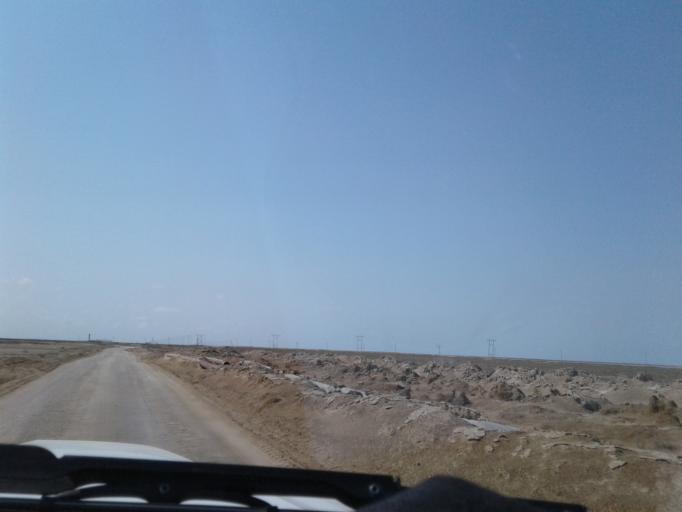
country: IR
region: Golestan
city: Gomishan
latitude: 37.8260
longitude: 53.9215
